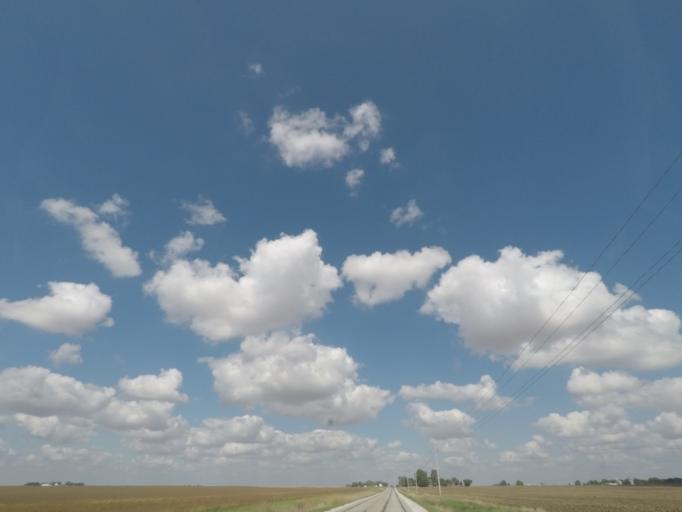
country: US
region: Iowa
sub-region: Story County
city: Nevada
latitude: 42.0573
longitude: -93.4057
